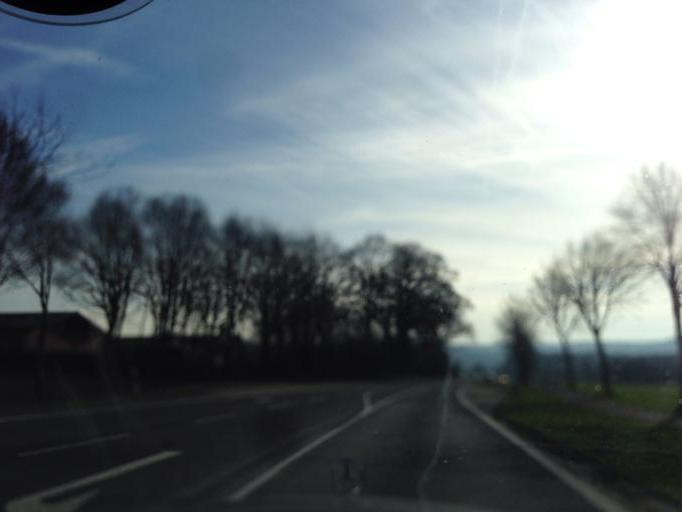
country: DE
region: North Rhine-Westphalia
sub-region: Regierungsbezirk Munster
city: Tecklenburg
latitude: 52.2500
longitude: 7.7979
